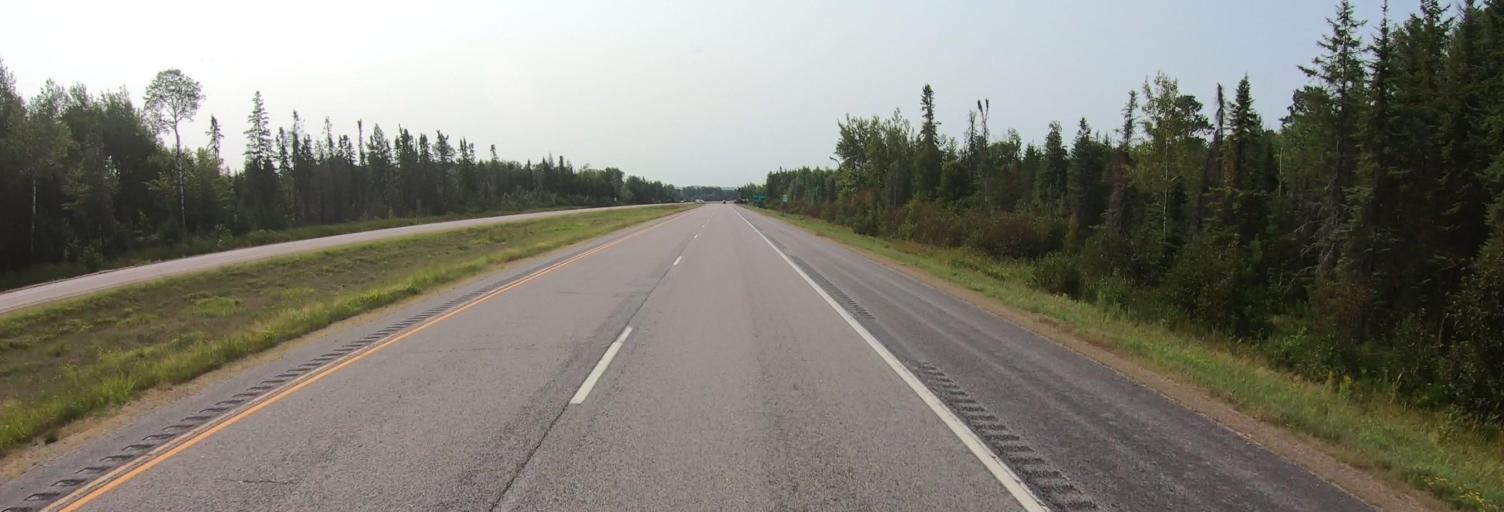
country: US
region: Minnesota
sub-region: Saint Louis County
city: Parkville
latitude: 47.6415
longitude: -92.5628
